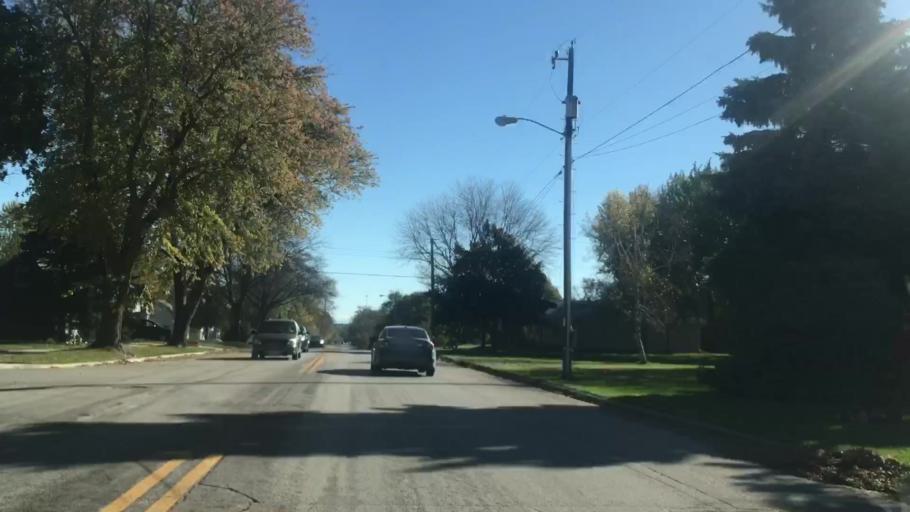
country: US
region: Wisconsin
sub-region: Waukesha County
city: Menomonee Falls
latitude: 43.1703
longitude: -88.1146
